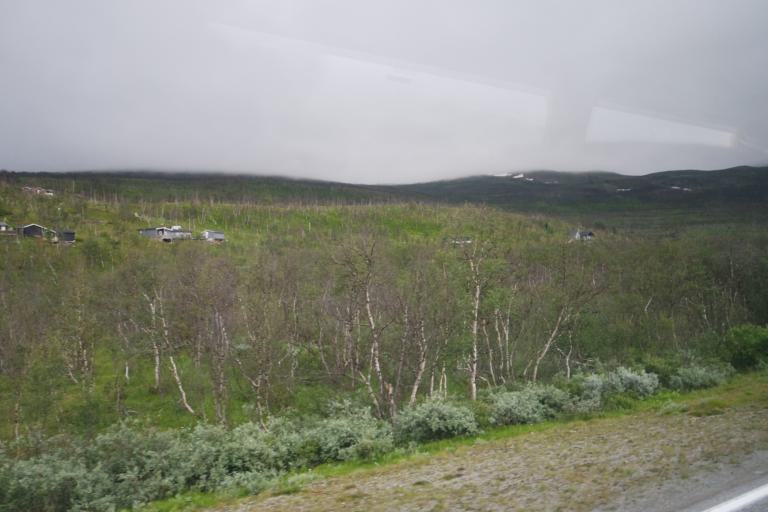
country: NO
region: Finnmark Fylke
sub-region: Kvalsund
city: Kvalsund
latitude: 70.3523
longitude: 24.3578
